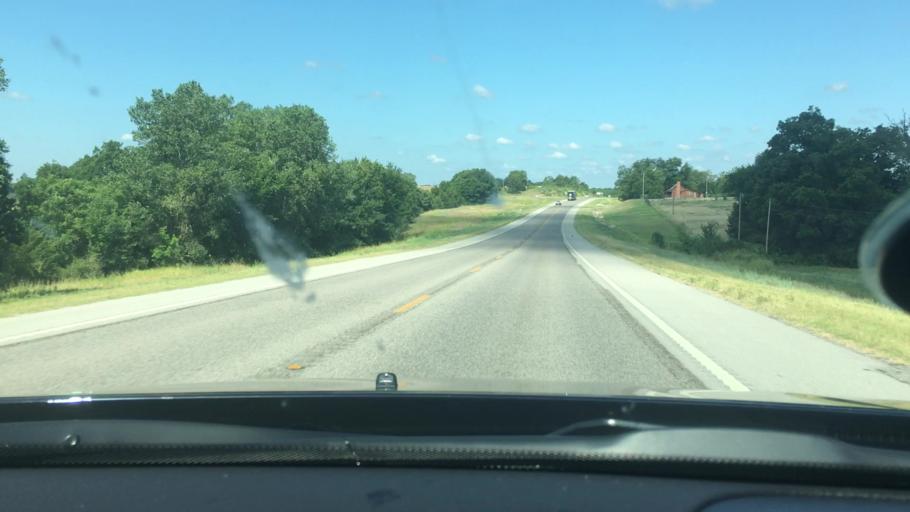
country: US
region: Oklahoma
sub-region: Carter County
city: Dickson
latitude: 34.1003
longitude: -96.9599
